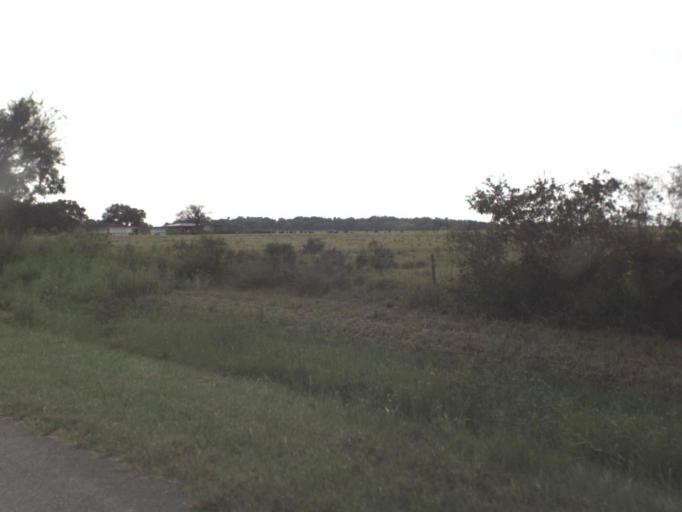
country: US
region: Florida
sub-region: Okeechobee County
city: Cypress Quarters
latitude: 27.4062
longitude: -80.8145
